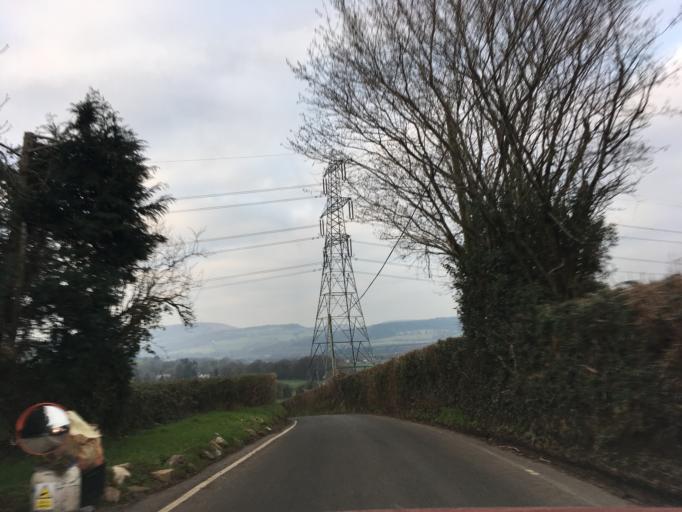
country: GB
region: Wales
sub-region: Newport
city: Marshfield
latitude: 51.5576
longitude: -3.0965
